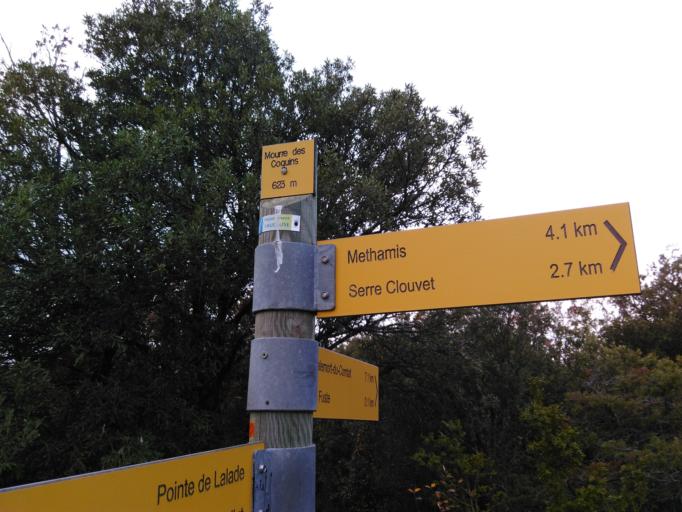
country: FR
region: Provence-Alpes-Cote d'Azur
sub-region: Departement du Vaucluse
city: Villes-sur-Auzon
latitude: 43.9857
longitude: 5.2242
